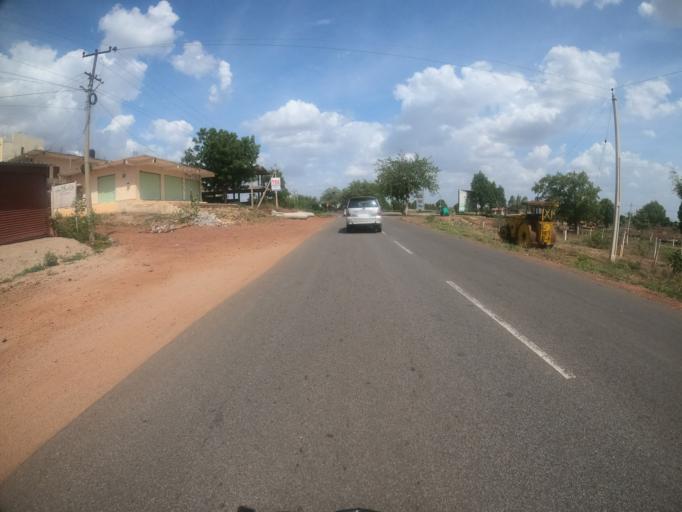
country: IN
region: Telangana
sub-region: Rangareddi
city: Sriramnagar
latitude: 17.3187
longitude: 78.1241
